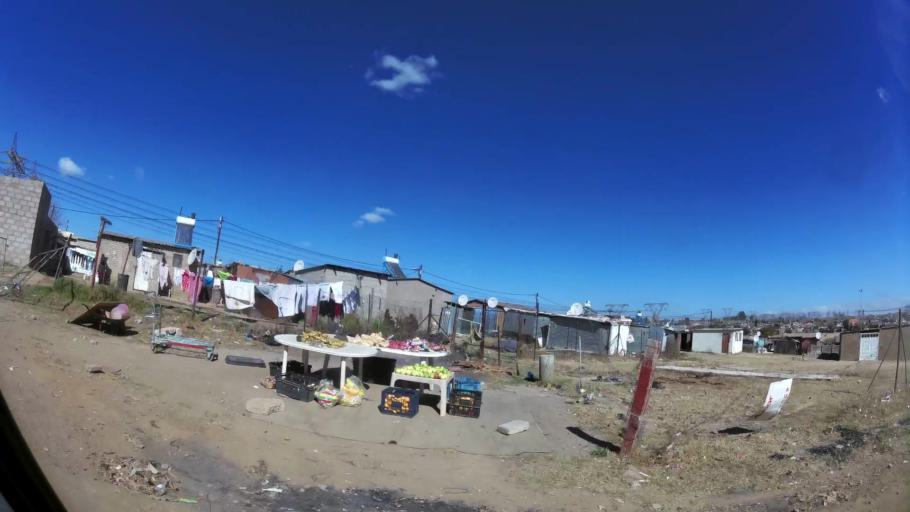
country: ZA
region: Gauteng
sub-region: City of Johannesburg Metropolitan Municipality
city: Midrand
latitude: -25.9189
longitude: 28.0979
